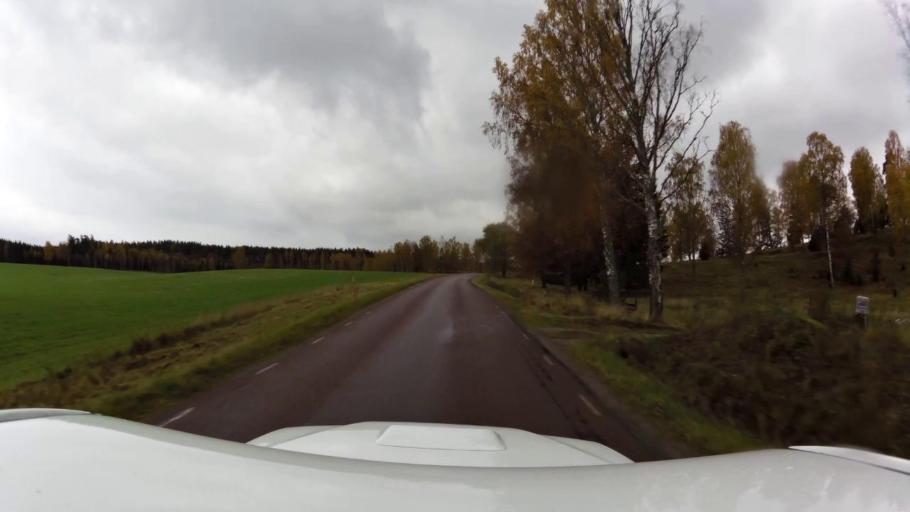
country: SE
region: OEstergoetland
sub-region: Linkopings Kommun
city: Ljungsbro
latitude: 58.5345
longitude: 15.5249
